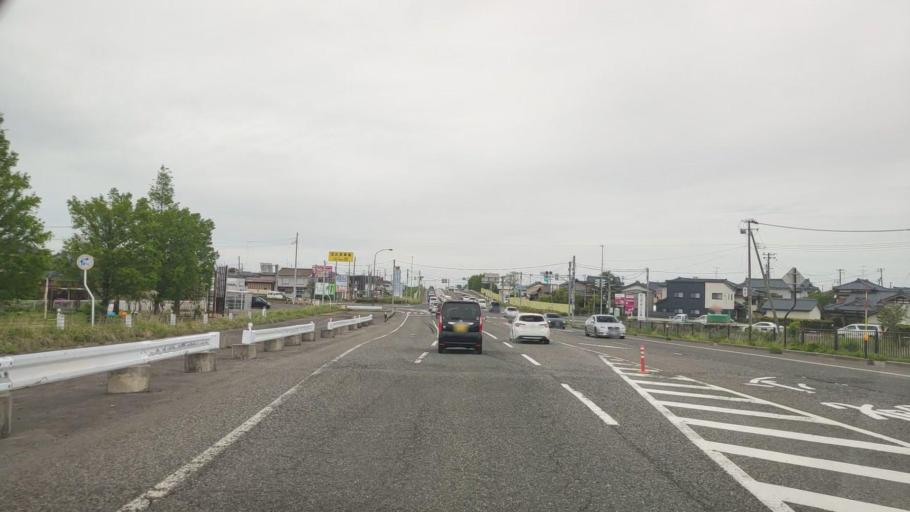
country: JP
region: Niigata
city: Niitsu-honcho
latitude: 37.7933
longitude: 139.1101
